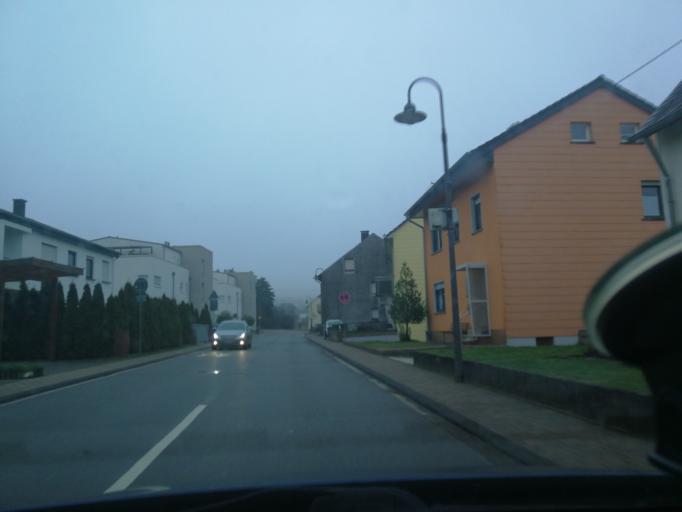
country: DE
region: Rheinland-Pfalz
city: Trierweiler
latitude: 49.7607
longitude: 6.5589
